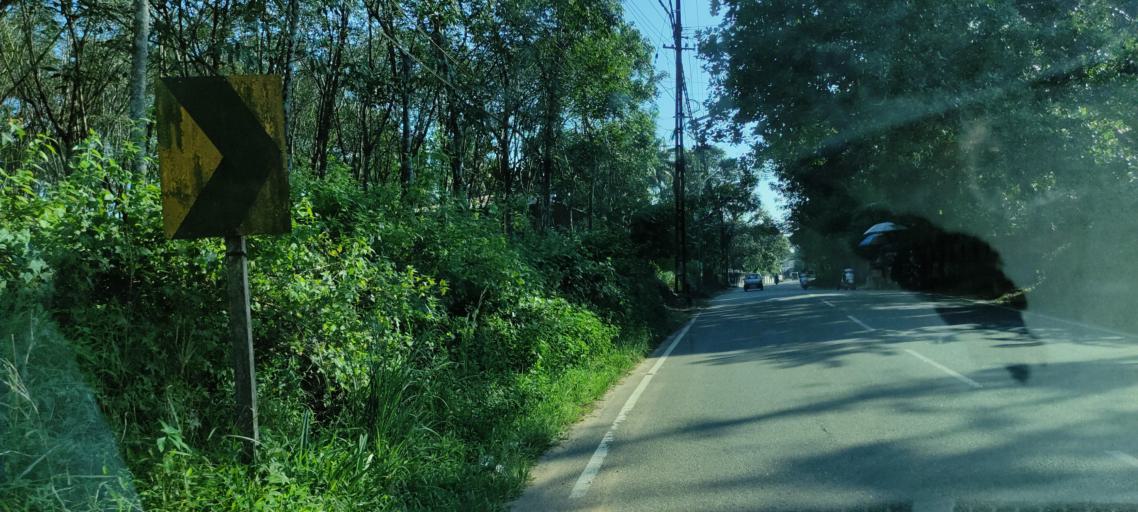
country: IN
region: Kerala
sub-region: Pattanamtitta
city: Adur
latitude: 9.1705
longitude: 76.7418
